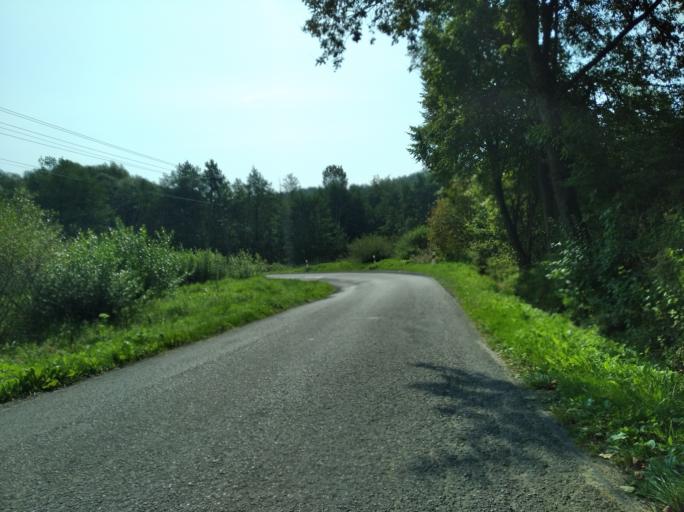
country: PL
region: Subcarpathian Voivodeship
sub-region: Powiat przeworski
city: Jawornik Polski
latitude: 49.8906
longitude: 22.2645
